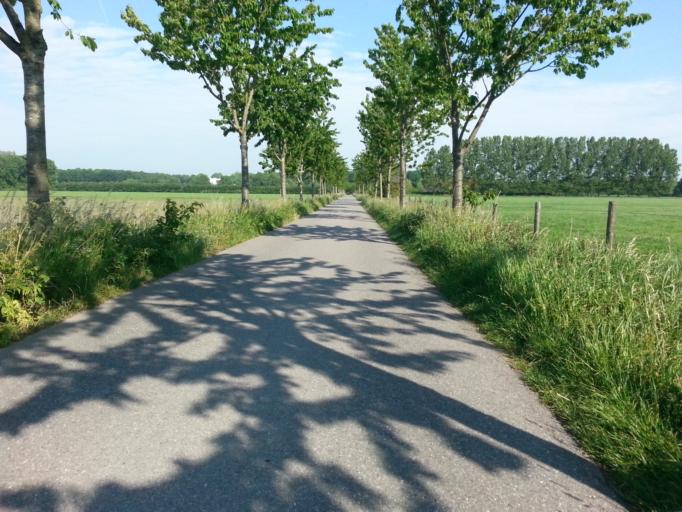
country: NL
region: Utrecht
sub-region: Gemeente Utrechtse Heuvelrug
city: Driebergen-Rijsenburg
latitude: 52.0270
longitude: 5.2598
